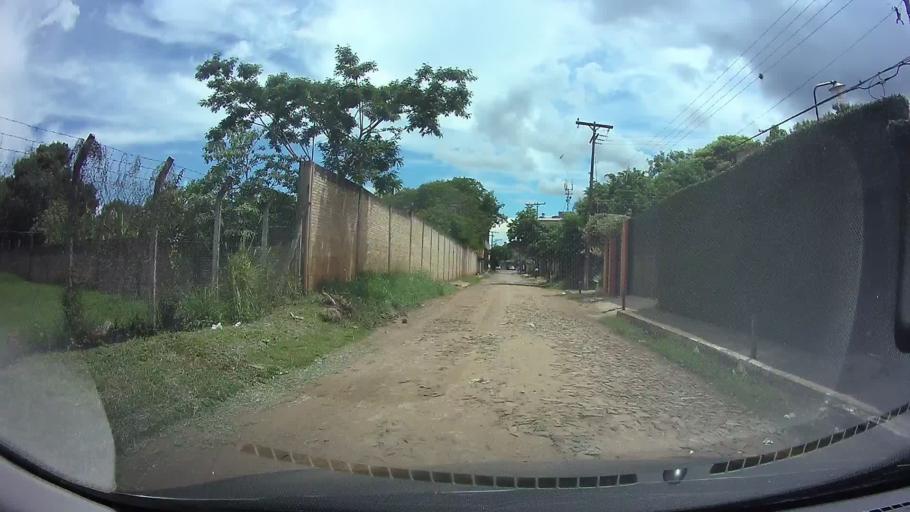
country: PY
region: Central
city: Fernando de la Mora
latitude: -25.3153
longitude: -57.5249
